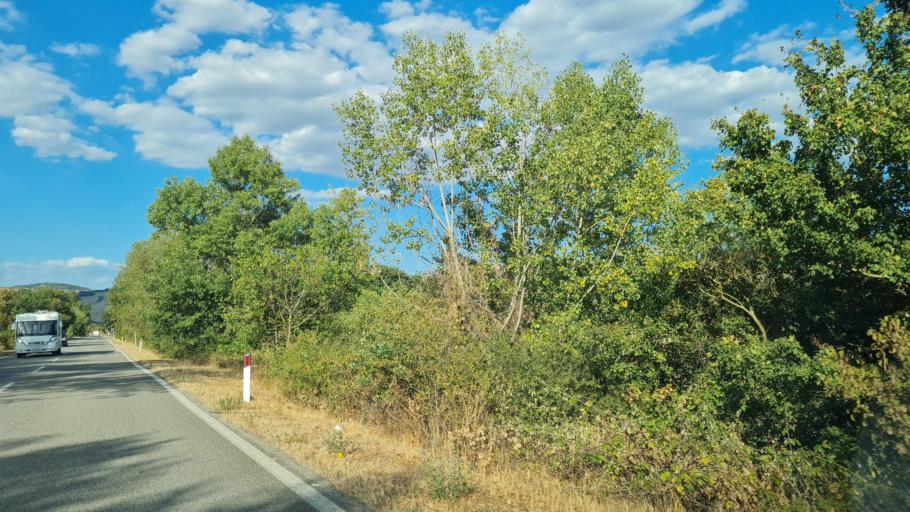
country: IT
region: Tuscany
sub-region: Provincia di Siena
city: Pienza
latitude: 42.9919
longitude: 11.7196
